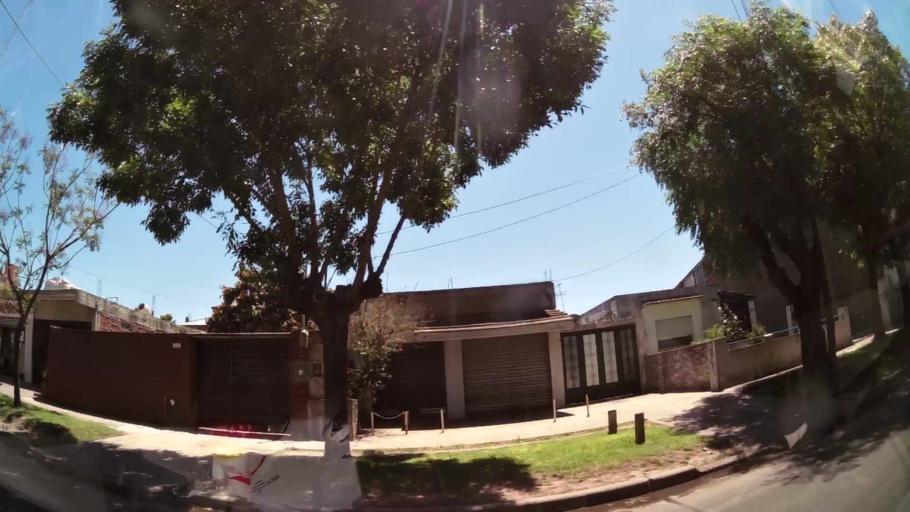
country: AR
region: Buenos Aires
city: Hurlingham
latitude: -34.5045
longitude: -58.6973
